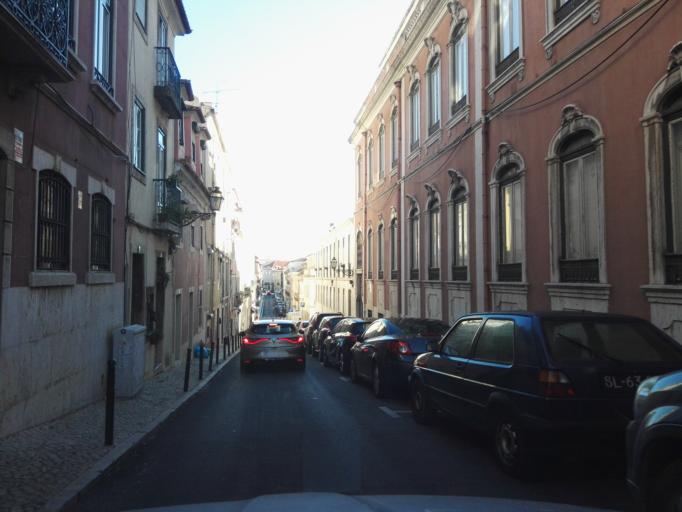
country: PT
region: Lisbon
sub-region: Lisbon
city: Lisbon
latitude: 38.7161
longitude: -9.1505
